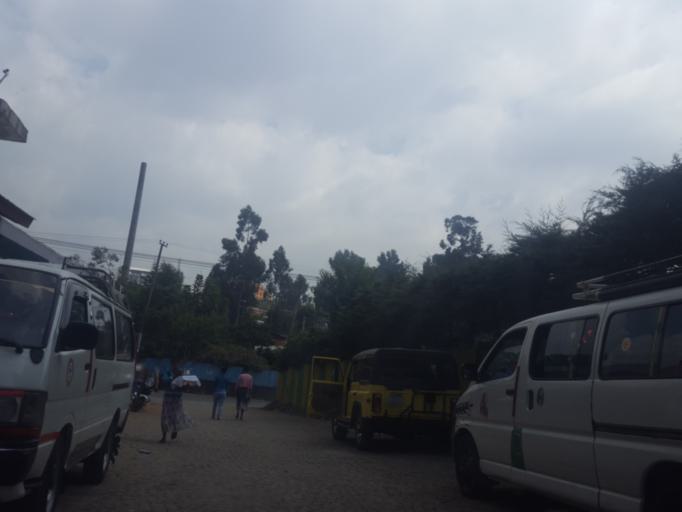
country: ET
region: Adis Abeba
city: Addis Ababa
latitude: 9.0636
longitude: 38.7265
